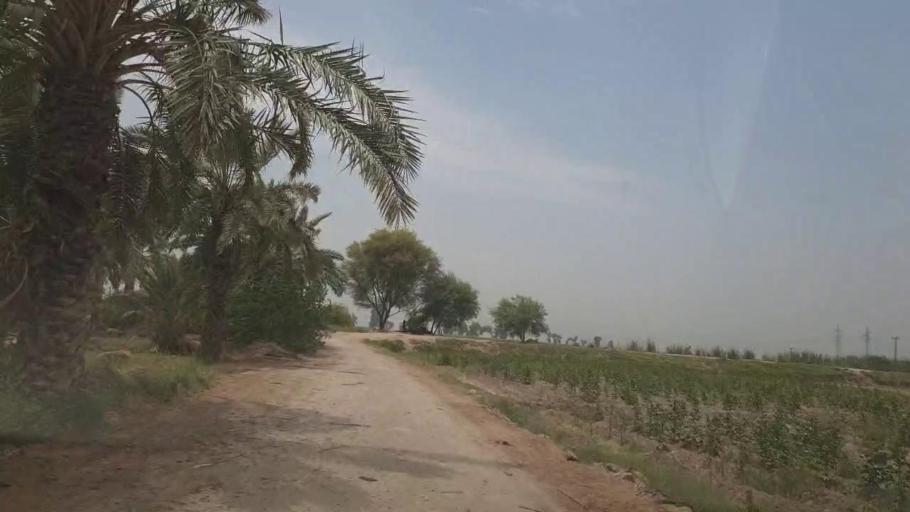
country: PK
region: Sindh
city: Kot Diji
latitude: 27.4441
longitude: 68.6777
